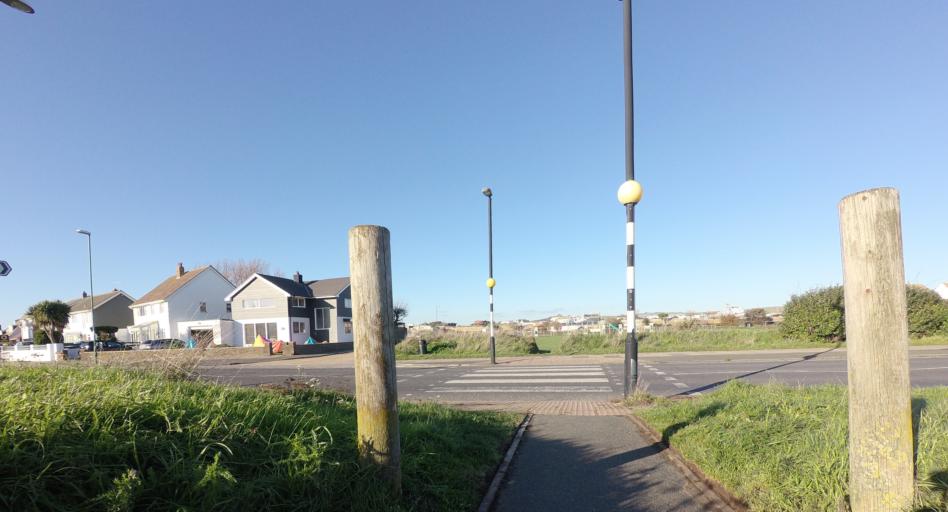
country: GB
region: England
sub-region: West Sussex
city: Shoreham-by-Sea
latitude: 50.8277
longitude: -0.2796
